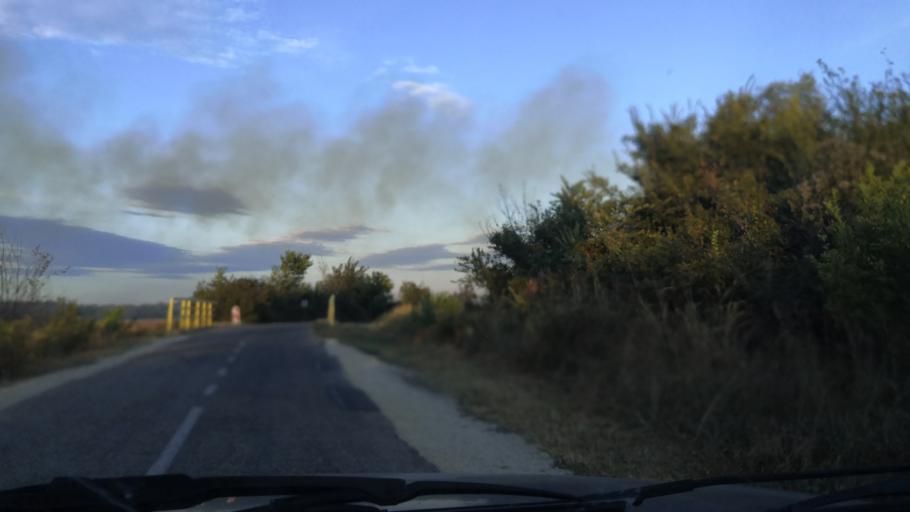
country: RS
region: Central Serbia
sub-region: Borski Okrug
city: Negotin
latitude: 44.2501
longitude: 22.5881
